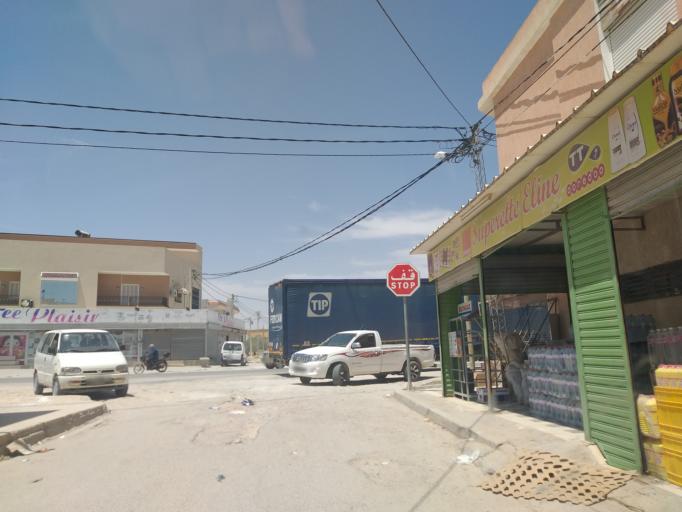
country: TN
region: Al Mahdiyah
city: El Jem
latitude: 35.2953
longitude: 10.6928
